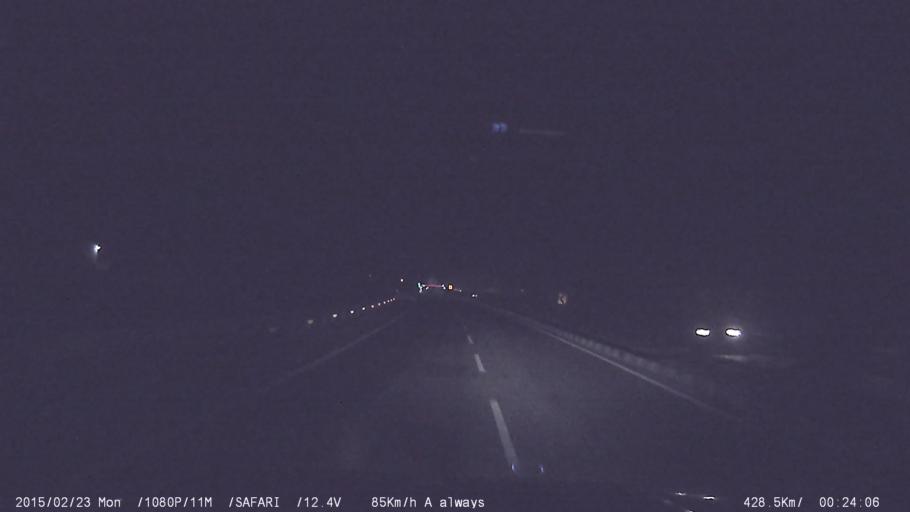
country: IN
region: Tamil Nadu
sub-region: Dharmapuri
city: Mallapuram
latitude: 11.9323
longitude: 78.0646
